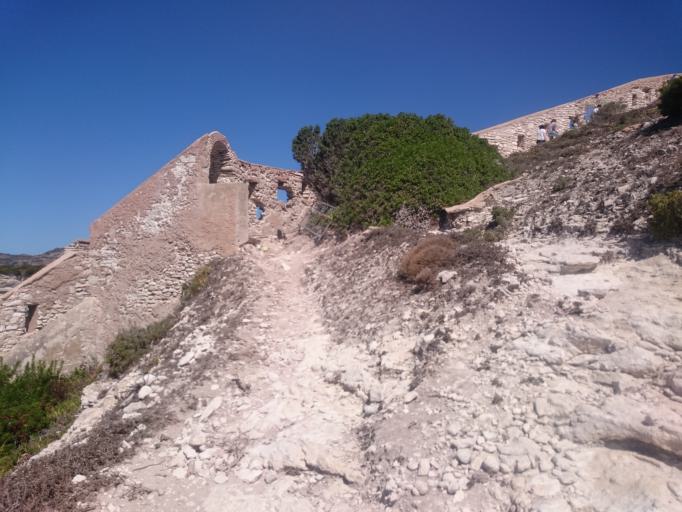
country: FR
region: Corsica
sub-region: Departement de la Corse-du-Sud
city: Bonifacio
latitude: 41.3865
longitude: 9.1488
